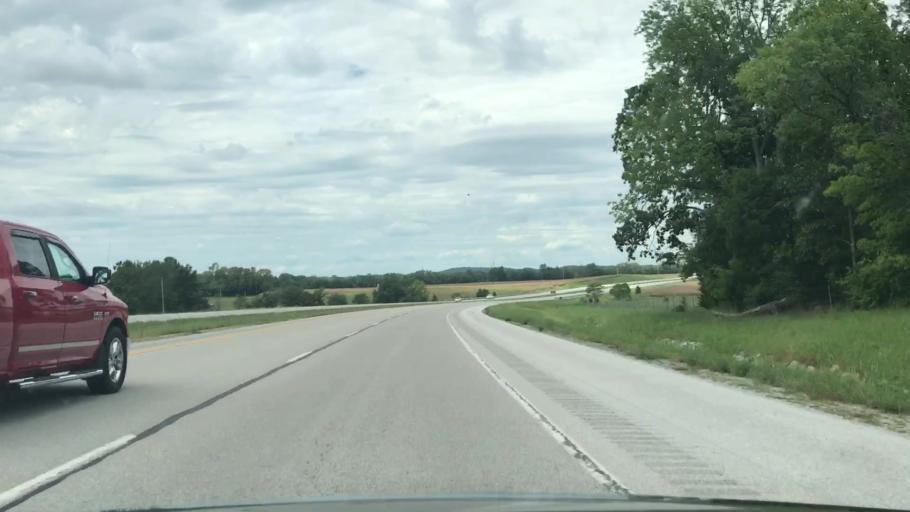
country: US
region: Kentucky
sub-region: Todd County
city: Elkton
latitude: 36.8092
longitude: -87.1316
